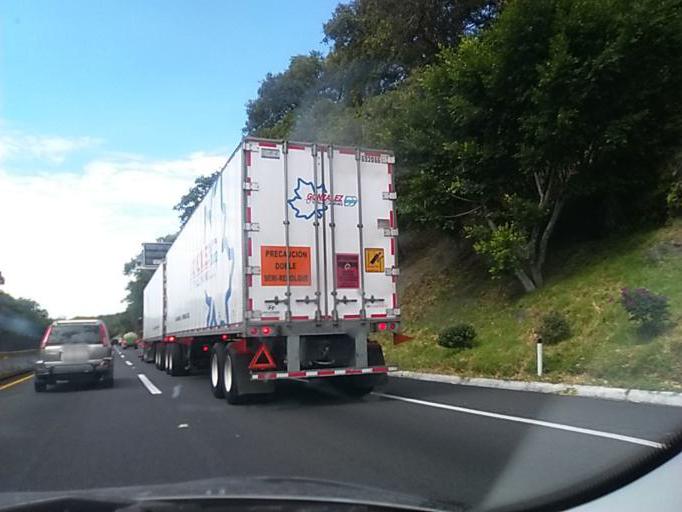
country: MX
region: Morelos
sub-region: Cuernavaca
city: Villa Santiago
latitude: 19.0038
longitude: -99.1867
